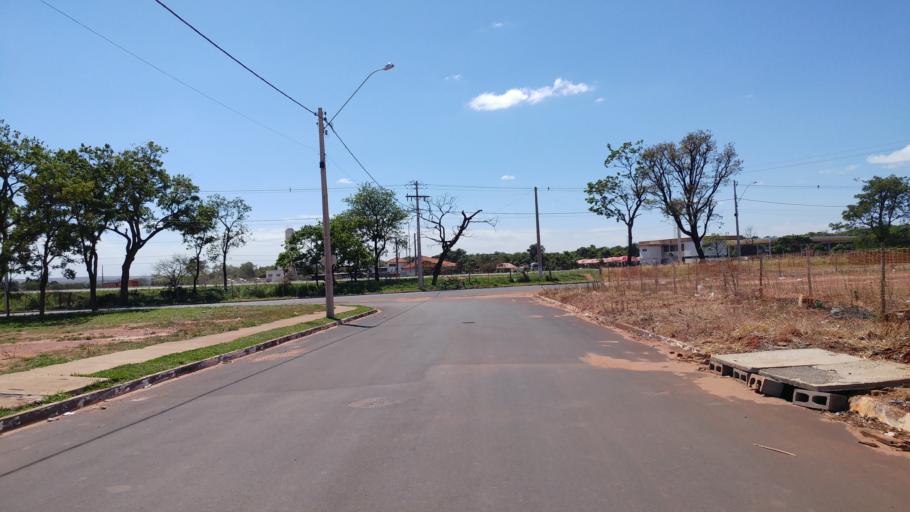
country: BR
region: Sao Paulo
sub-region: Paraguacu Paulista
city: Paraguacu Paulista
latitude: -22.4435
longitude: -50.5848
